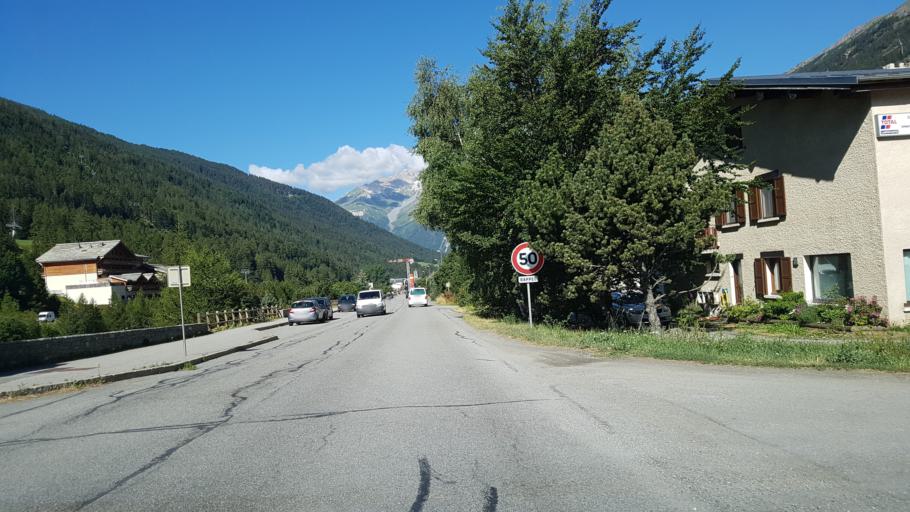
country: IT
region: Piedmont
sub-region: Provincia di Torino
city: Moncenisio
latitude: 45.2862
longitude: 6.8831
